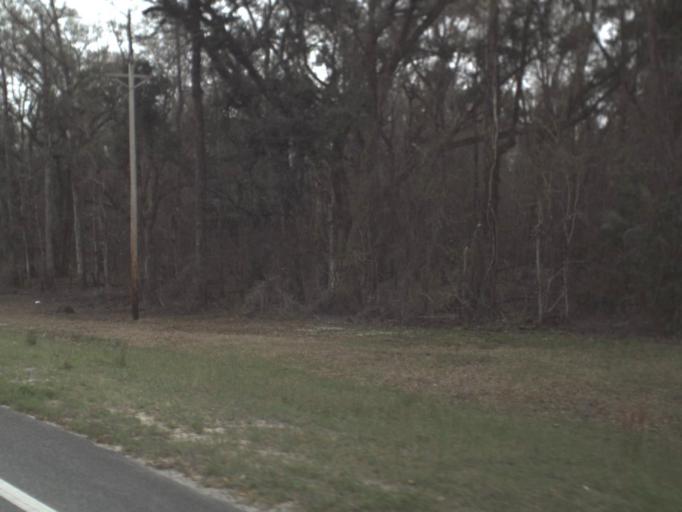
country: US
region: Florida
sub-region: Wakulla County
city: Crawfordville
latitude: 30.1374
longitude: -84.3271
